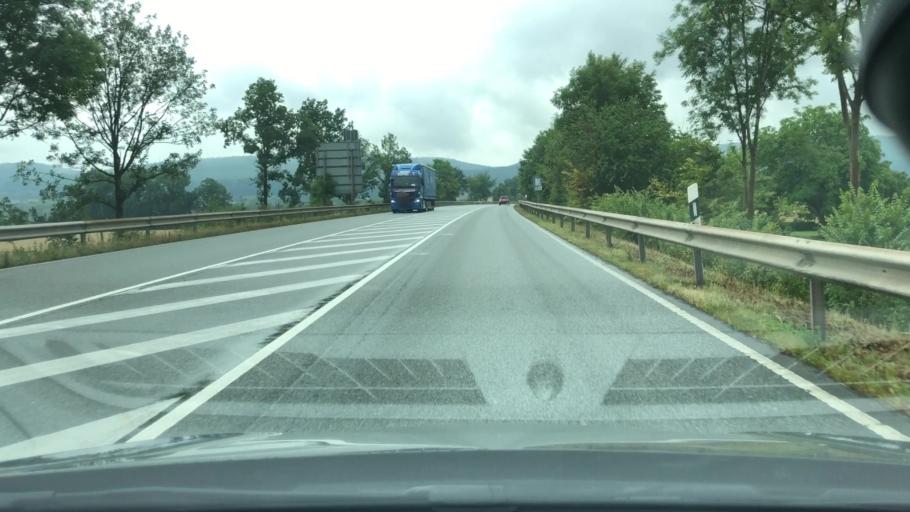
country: DE
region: North Rhine-Westphalia
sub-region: Regierungsbezirk Detmold
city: Minden
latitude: 52.2677
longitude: 8.9631
